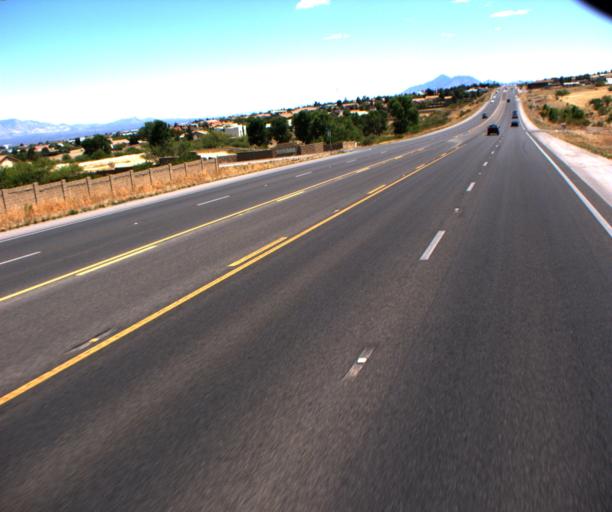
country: US
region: Arizona
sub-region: Cochise County
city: Sierra Vista Southeast
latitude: 31.4437
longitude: -110.2548
